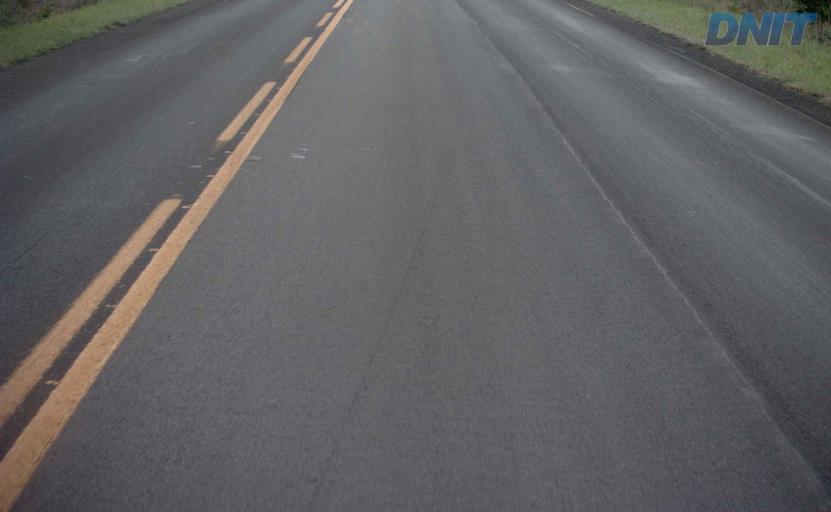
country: BR
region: Goias
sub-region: Padre Bernardo
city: Padre Bernardo
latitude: -15.2065
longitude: -48.4650
